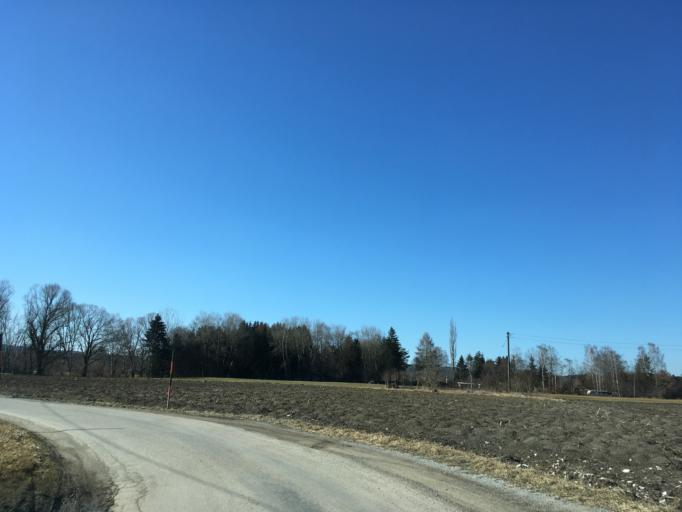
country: DE
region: Bavaria
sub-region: Upper Bavaria
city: Bad Aibling
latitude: 47.8229
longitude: 12.0050
